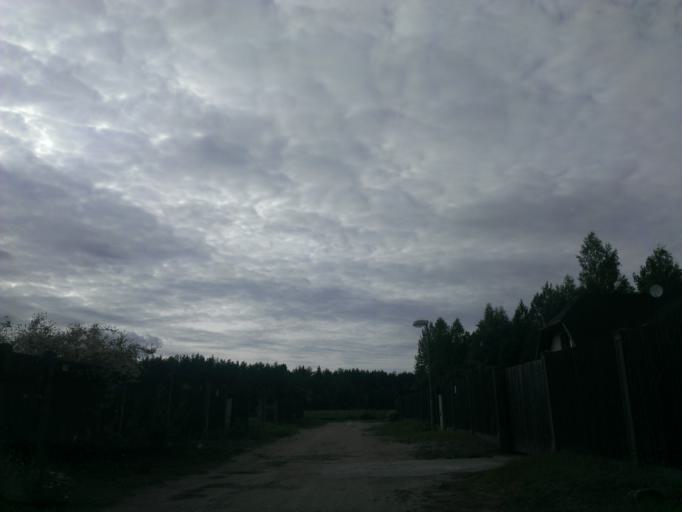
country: LV
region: Incukalns
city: Vangazi
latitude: 57.0961
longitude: 24.5593
